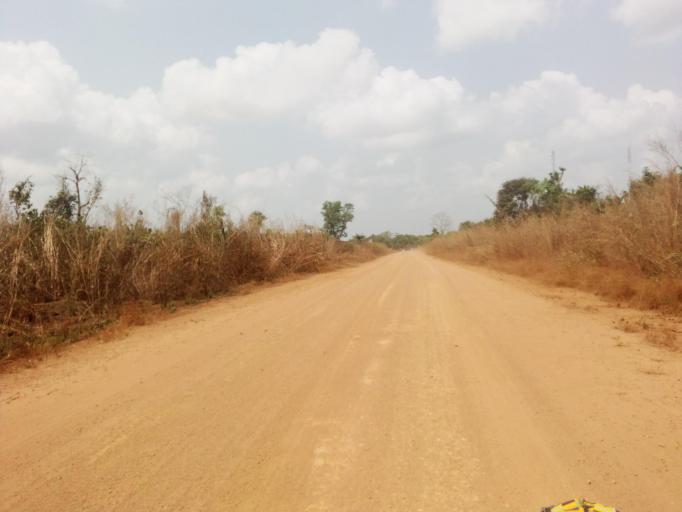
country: SL
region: Southern Province
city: Mogbwemo
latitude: 7.6632
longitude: -12.2714
